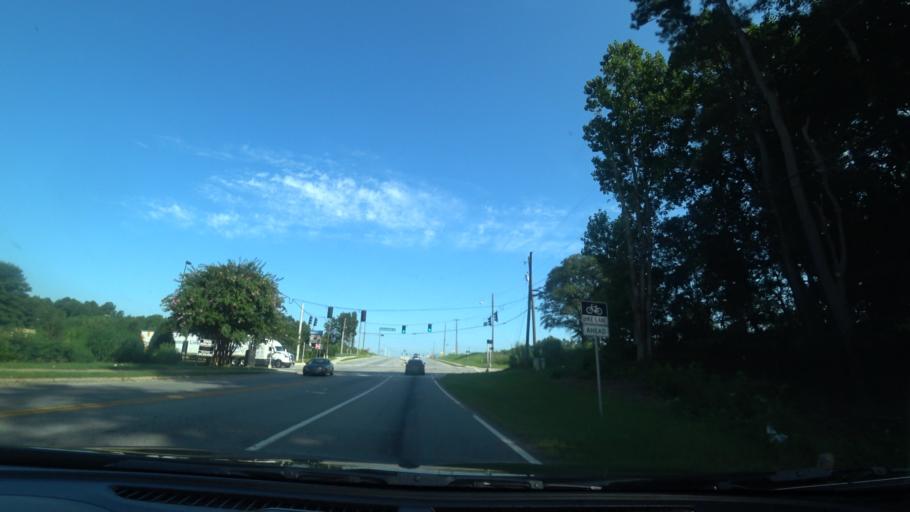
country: US
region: Georgia
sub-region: Gwinnett County
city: Lawrenceville
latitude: 33.9737
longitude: -83.9937
